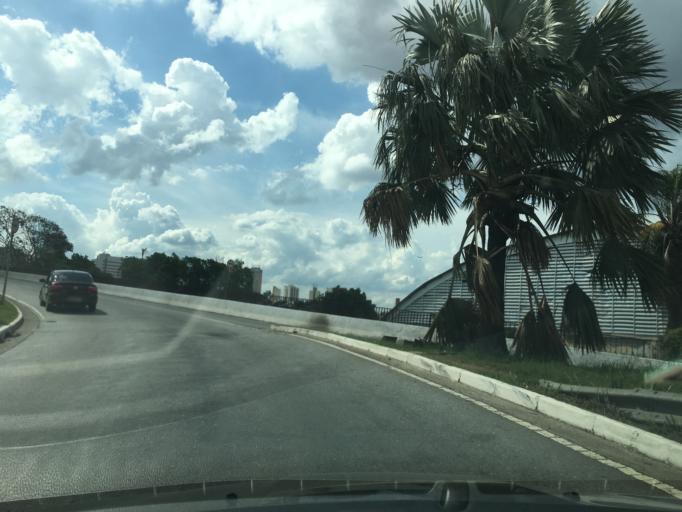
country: BR
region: Sao Paulo
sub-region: Guarulhos
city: Guarulhos
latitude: -23.4793
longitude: -46.5280
